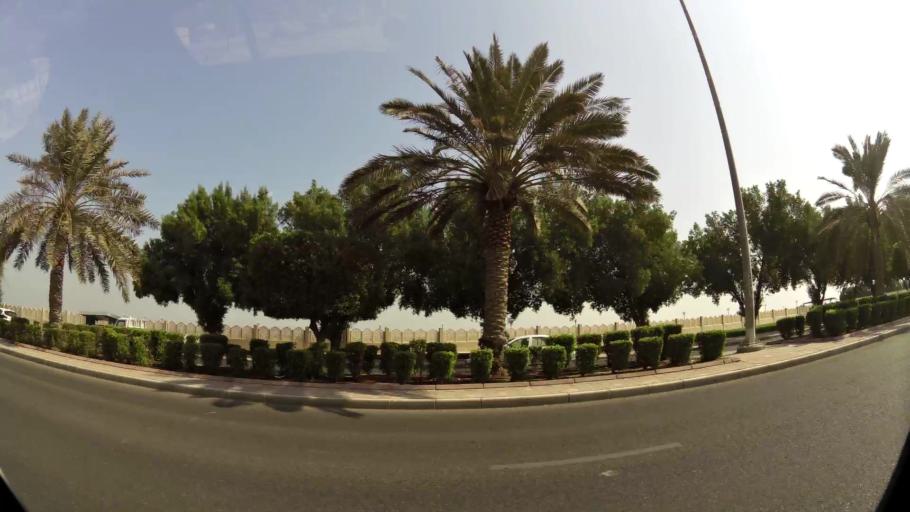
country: KW
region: Al Ahmadi
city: Al Fintas
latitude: 29.1736
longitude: 48.1225
